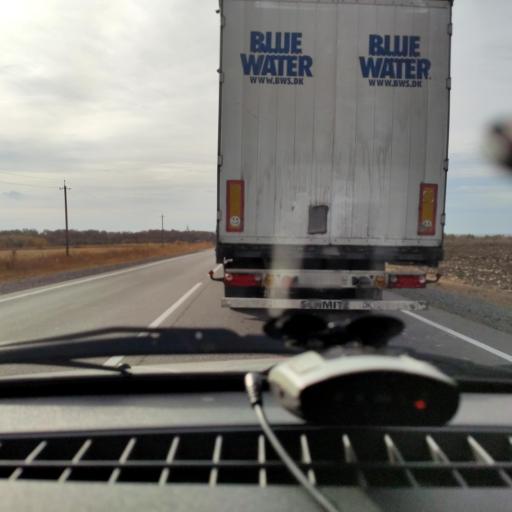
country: RU
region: Voronezj
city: Strelitsa
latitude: 51.5258
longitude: 38.9687
